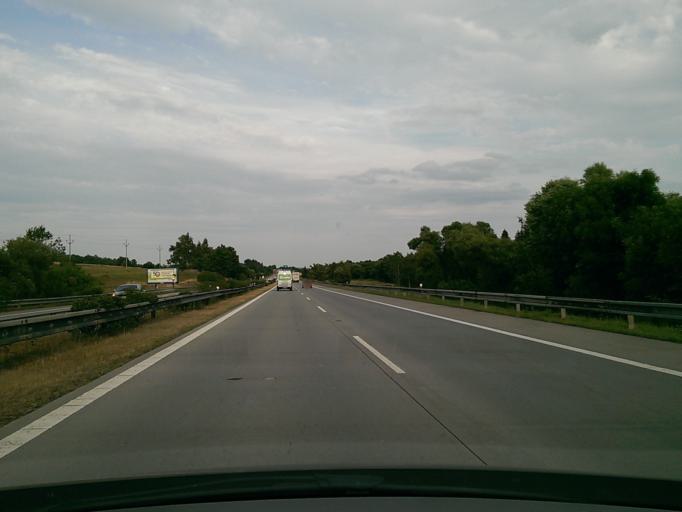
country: CZ
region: Vysocina
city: Merin
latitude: 49.4019
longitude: 15.8526
